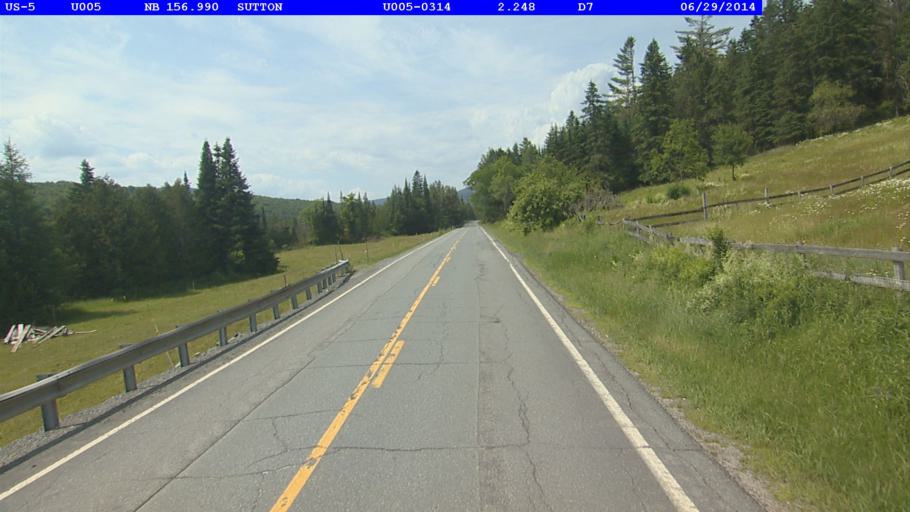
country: US
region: Vermont
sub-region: Caledonia County
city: Lyndonville
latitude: 44.6599
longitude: -72.0198
